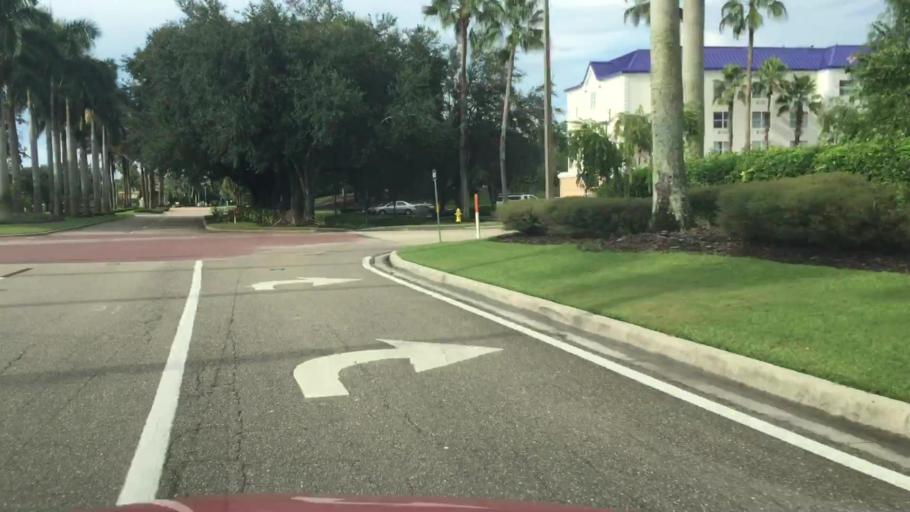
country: US
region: Florida
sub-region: Lee County
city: Gateway
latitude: 26.5480
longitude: -81.7997
